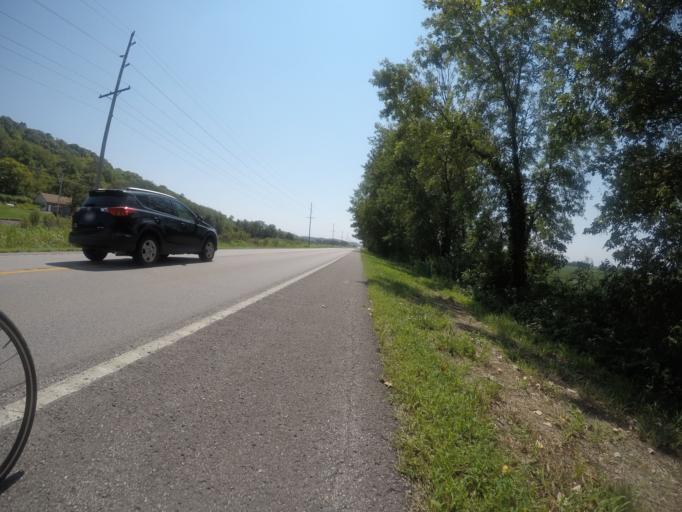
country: US
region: Kansas
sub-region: Atchison County
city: Atchison
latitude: 39.5297
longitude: -95.0345
